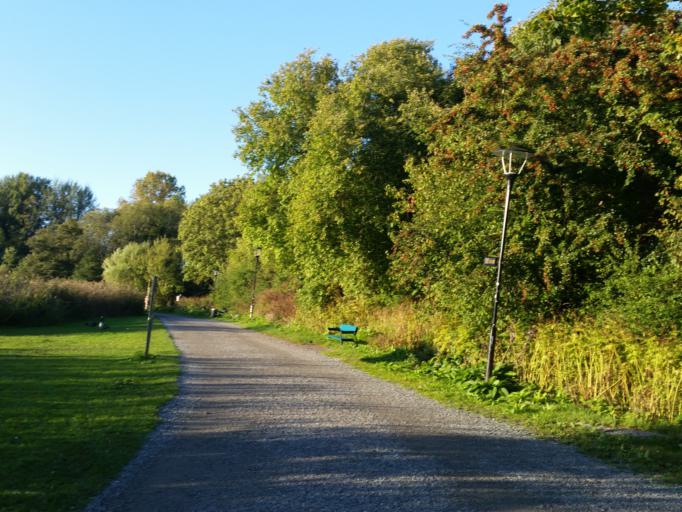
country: SE
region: Stockholm
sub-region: Solna Kommun
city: Solna
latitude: 59.3712
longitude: 17.9963
